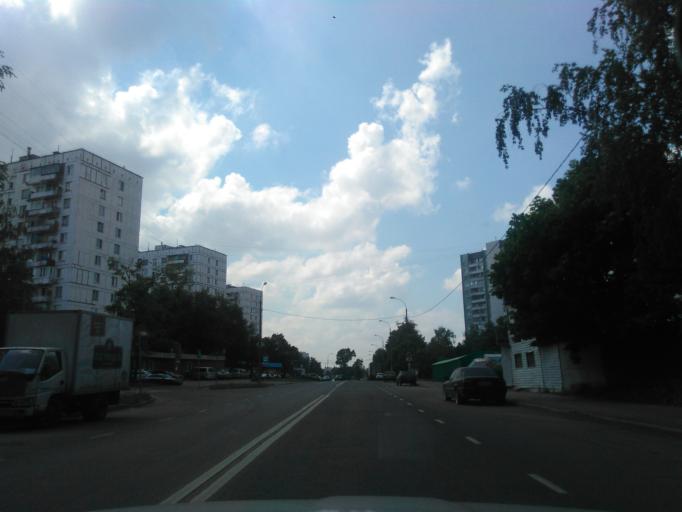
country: RU
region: Moscow
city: Businovo
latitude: 55.8853
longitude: 37.5215
